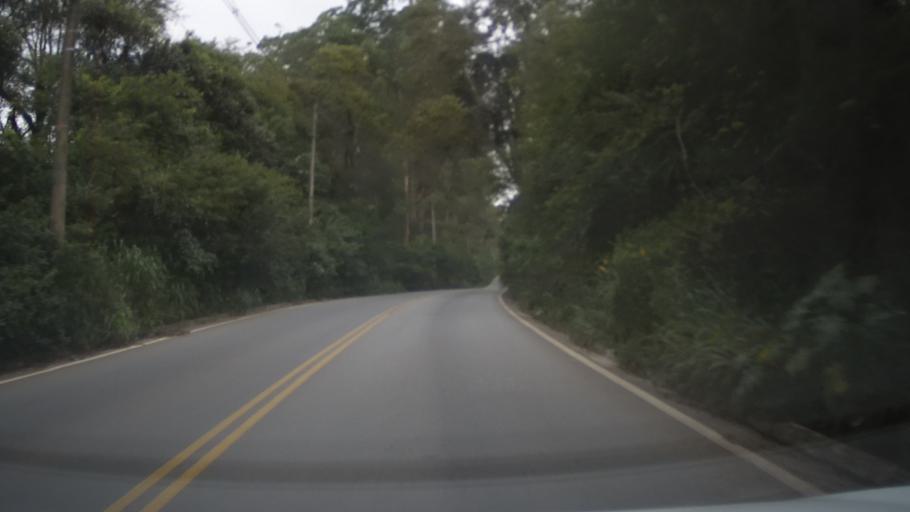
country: BR
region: Sao Paulo
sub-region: Aruja
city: Aruja
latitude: -23.3737
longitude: -46.4219
